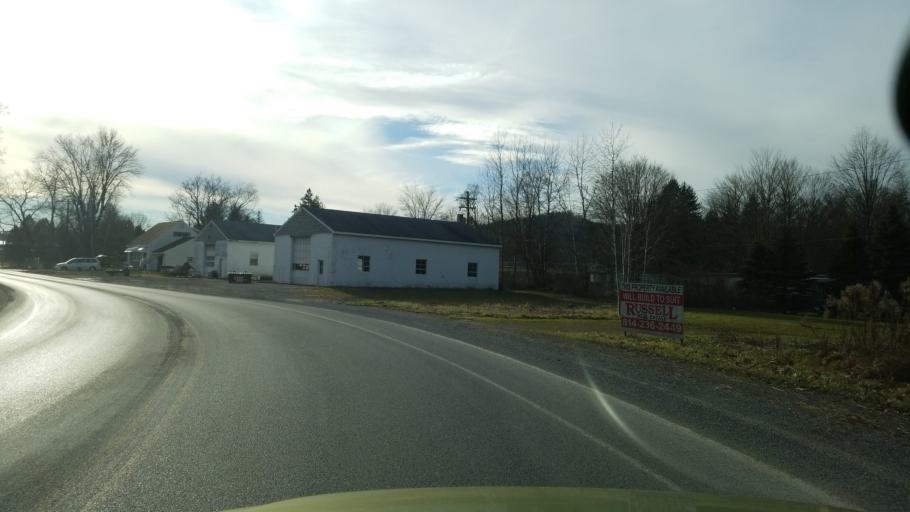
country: US
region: Pennsylvania
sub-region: Clearfield County
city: Hyde
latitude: 41.0056
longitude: -78.4607
